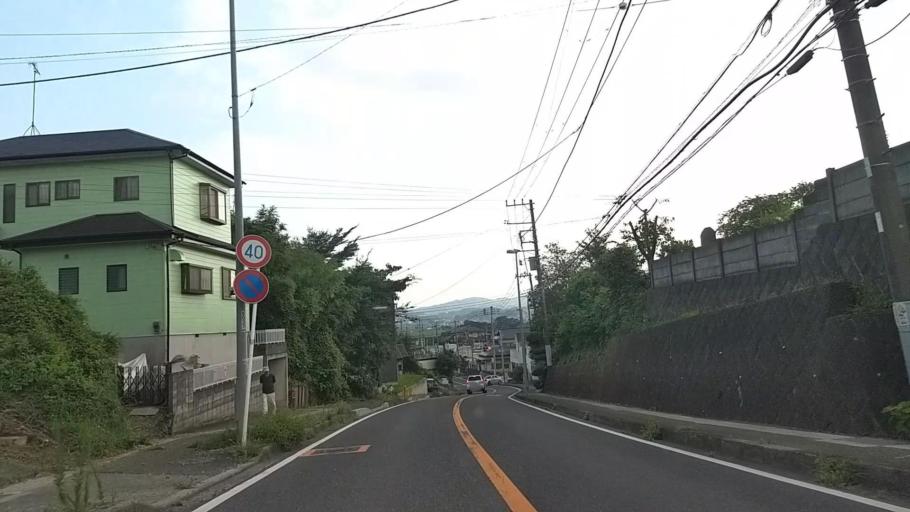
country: JP
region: Kanagawa
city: Isehara
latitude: 35.3758
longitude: 139.2998
